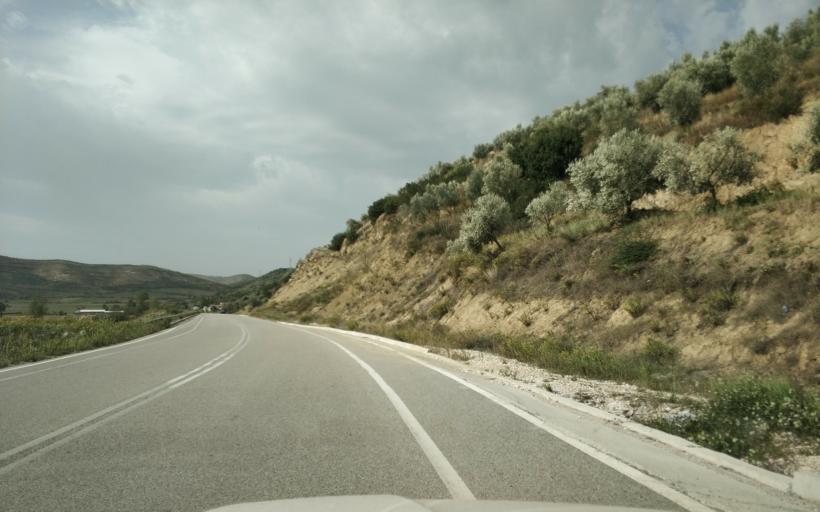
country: AL
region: Gjirokaster
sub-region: Rrethi i Tepelenes
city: Krahes
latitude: 40.3850
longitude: 19.8868
